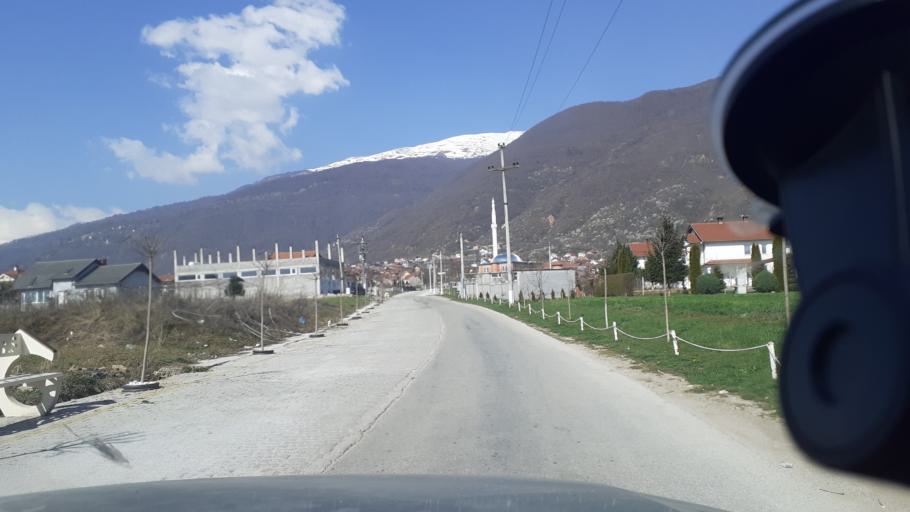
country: MK
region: Tearce
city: Tearce
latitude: 42.0690
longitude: 21.0503
